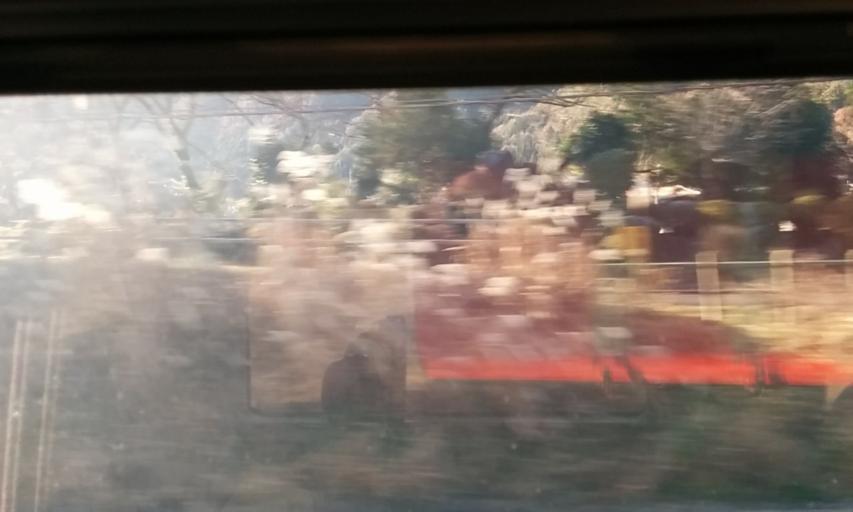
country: JP
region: Gifu
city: Nakatsugawa
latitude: 35.5958
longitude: 137.6079
